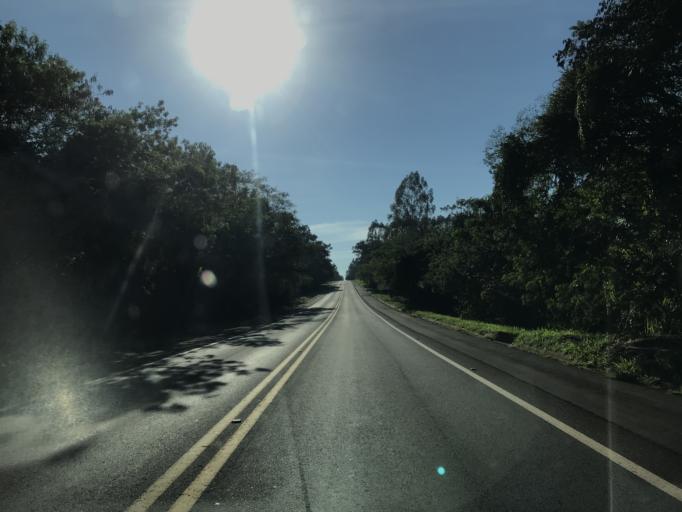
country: BR
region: Parana
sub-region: Ipora
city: Ipora
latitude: -24.0020
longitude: -53.6930
